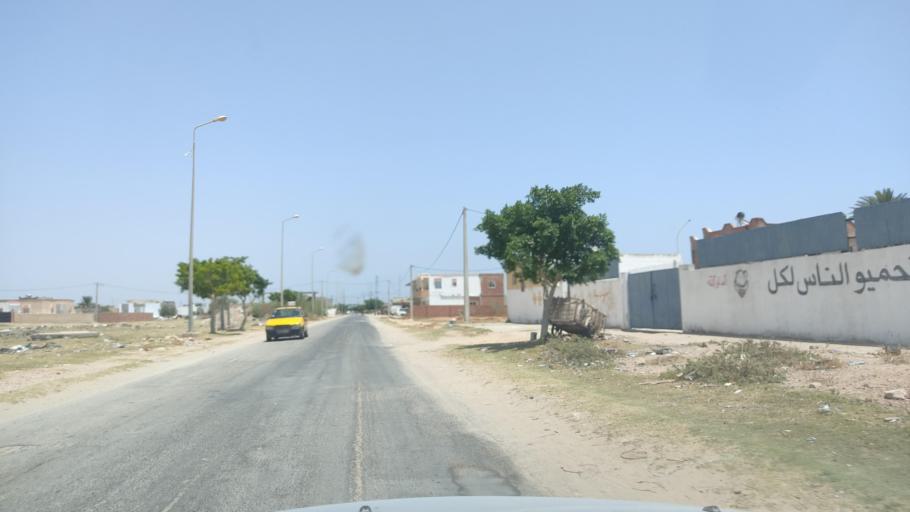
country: TN
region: Safaqis
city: Sfax
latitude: 34.6640
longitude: 10.7066
